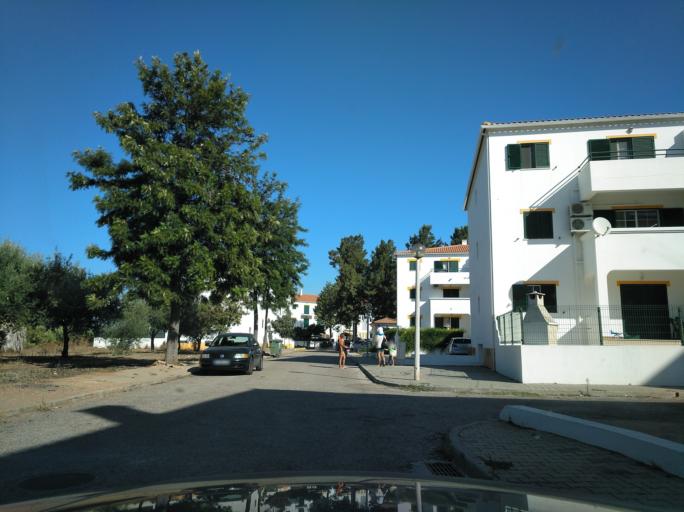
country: PT
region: Faro
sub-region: Vila Real de Santo Antonio
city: Monte Gordo
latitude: 37.1730
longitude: -7.5068
